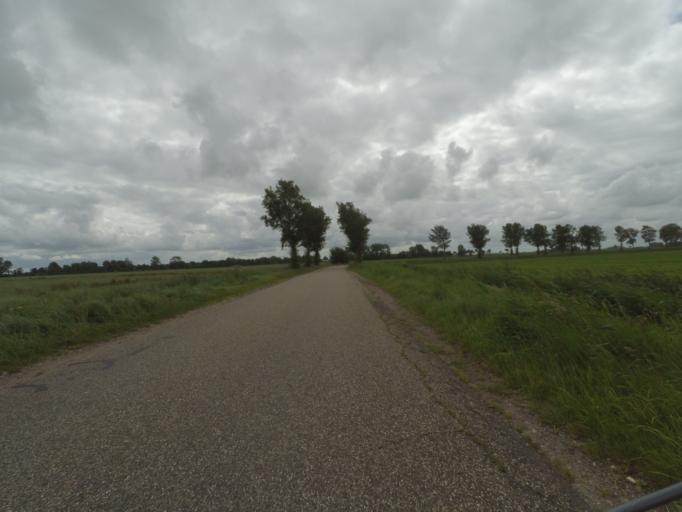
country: NL
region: Friesland
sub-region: Gemeente Kollumerland en Nieuwkruisland
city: Kollumerzwaag
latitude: 53.2999
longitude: 6.0869
